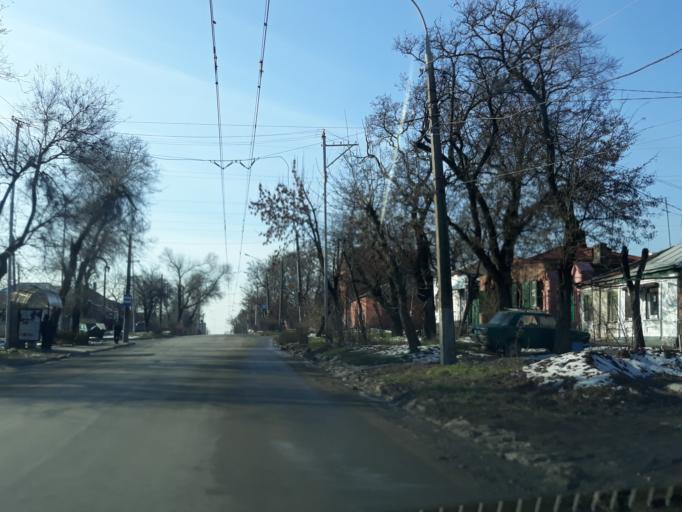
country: RU
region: Rostov
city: Taganrog
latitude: 47.2052
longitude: 38.9110
